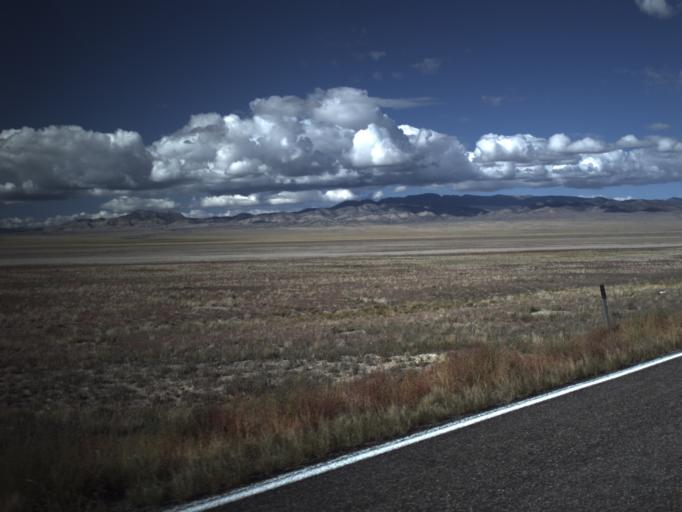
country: US
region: Utah
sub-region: Beaver County
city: Milford
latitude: 38.5181
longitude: -113.6434
